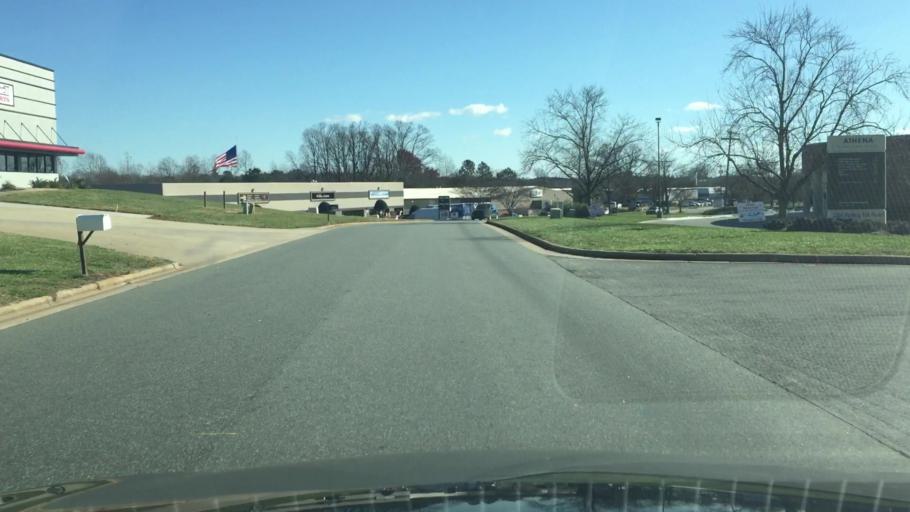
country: US
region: North Carolina
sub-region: Iredell County
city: Mooresville
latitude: 35.5879
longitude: -80.8623
